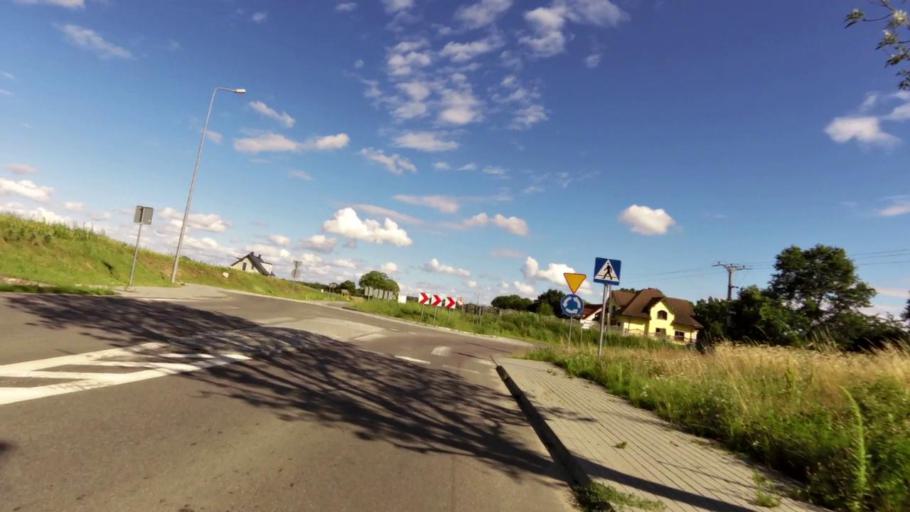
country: PL
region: West Pomeranian Voivodeship
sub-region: Powiat slawienski
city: Slawno
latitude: 54.4549
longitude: 16.7408
